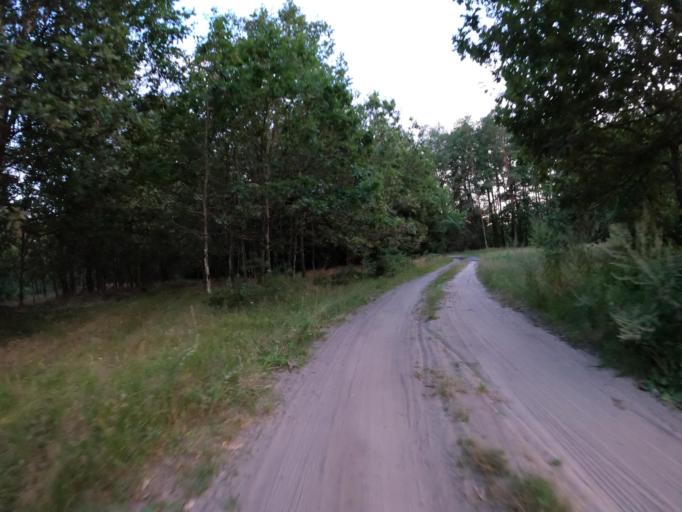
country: PL
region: West Pomeranian Voivodeship
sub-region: Powiat koszalinski
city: Sianow
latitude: 54.0819
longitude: 16.4005
